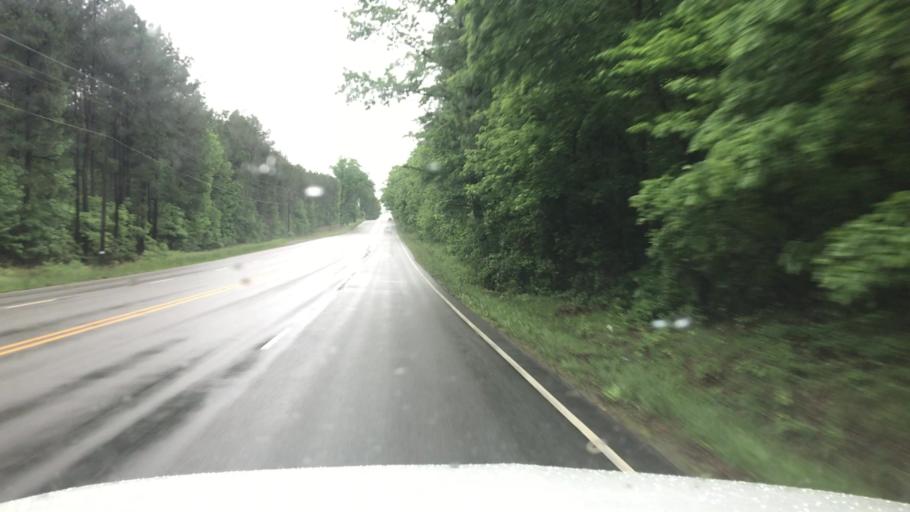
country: US
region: Virginia
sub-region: Hanover County
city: Ashland
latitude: 37.8380
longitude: -77.4673
